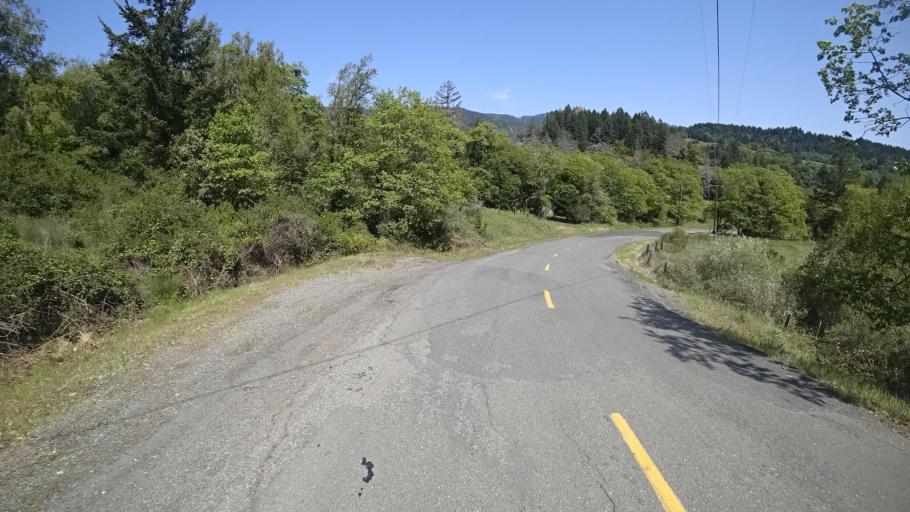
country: US
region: California
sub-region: Humboldt County
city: Redway
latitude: 40.2744
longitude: -123.6310
